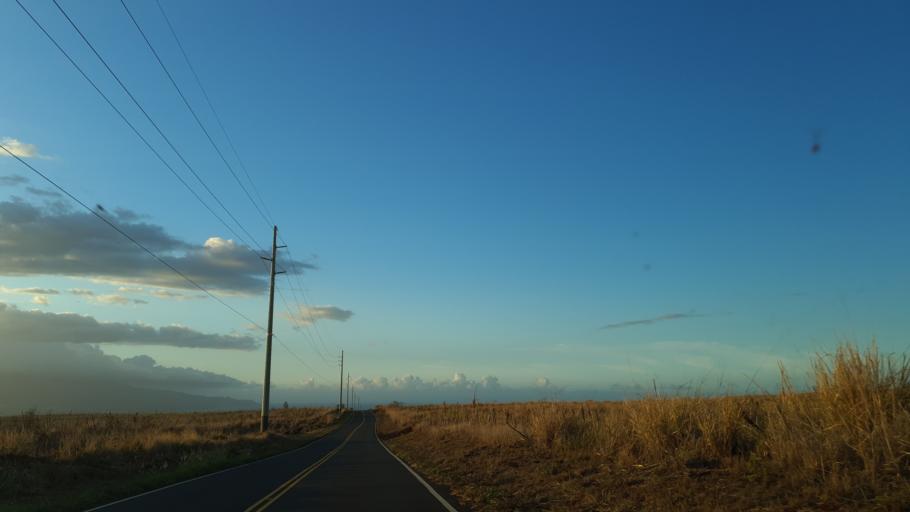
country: US
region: Hawaii
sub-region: Maui County
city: Pukalani
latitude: 20.8056
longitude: -156.3790
